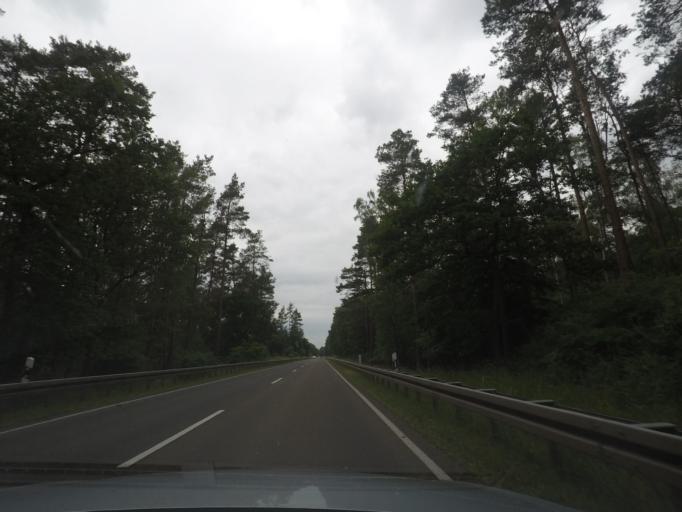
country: DE
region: Saxony-Anhalt
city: Colbitz
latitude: 52.3442
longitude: 11.5762
